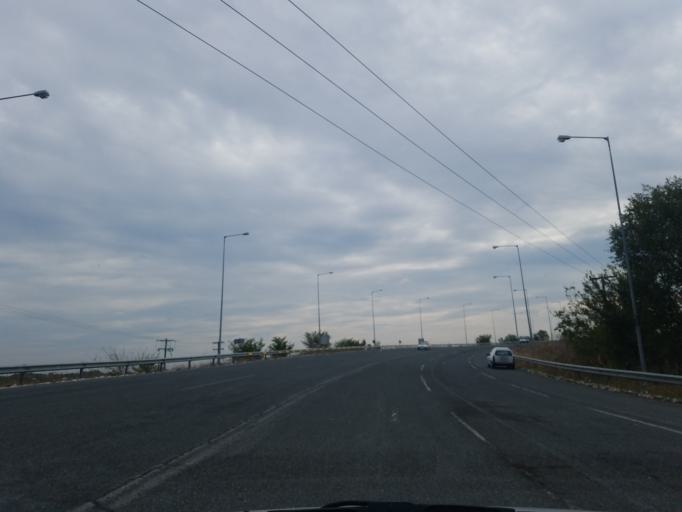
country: GR
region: Thessaly
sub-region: Nomos Kardhitsas
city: Sofades
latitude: 39.3437
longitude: 22.0801
